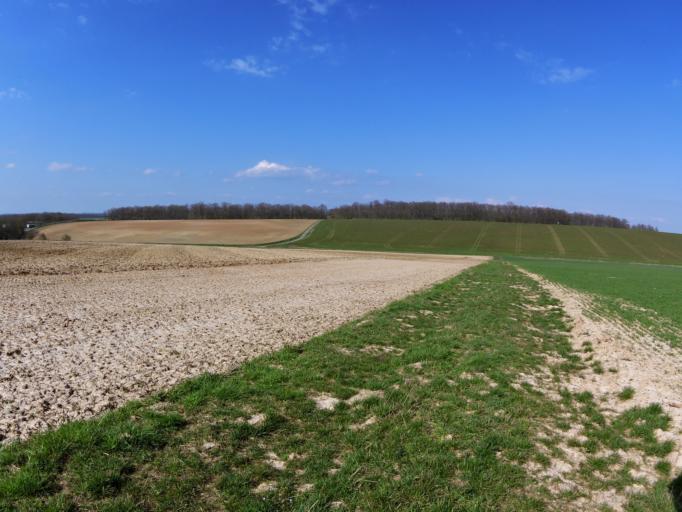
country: DE
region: Bavaria
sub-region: Regierungsbezirk Unterfranken
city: Rottendorf
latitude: 49.7977
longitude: 10.0568
